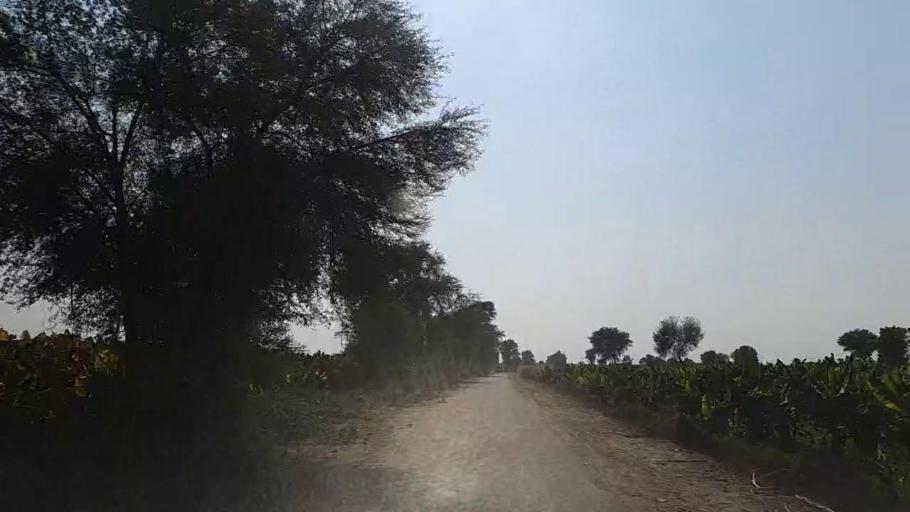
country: PK
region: Sindh
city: Daur
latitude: 26.4866
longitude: 68.2505
